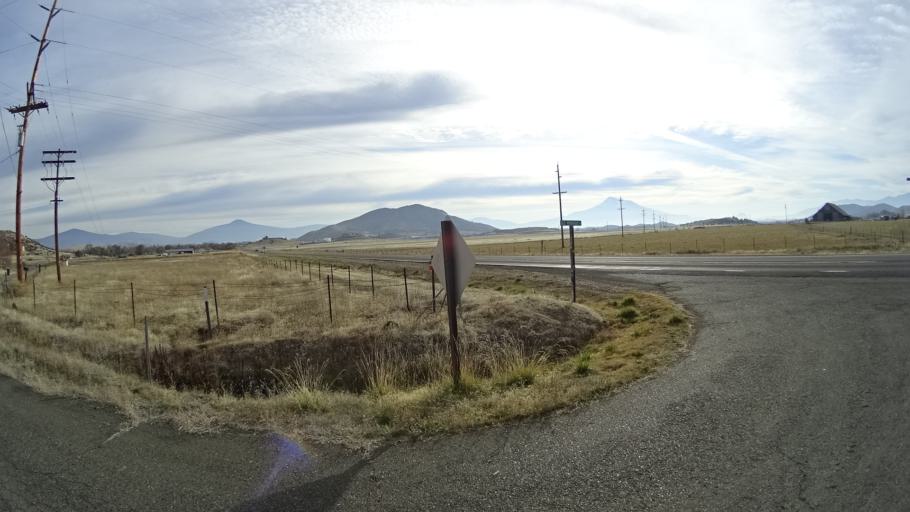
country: US
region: California
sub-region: Siskiyou County
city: Montague
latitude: 41.7249
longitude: -122.5464
